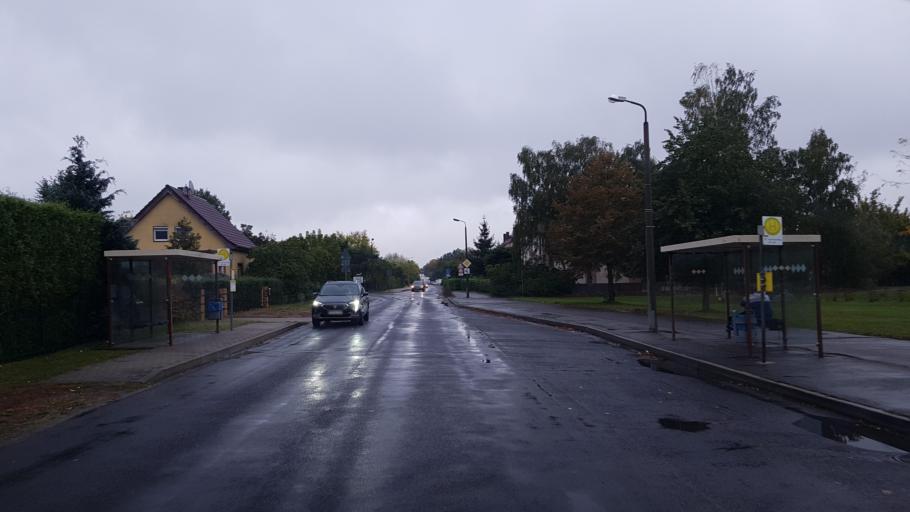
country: DE
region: Brandenburg
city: Furstenwalde
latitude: 52.3438
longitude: 14.0683
